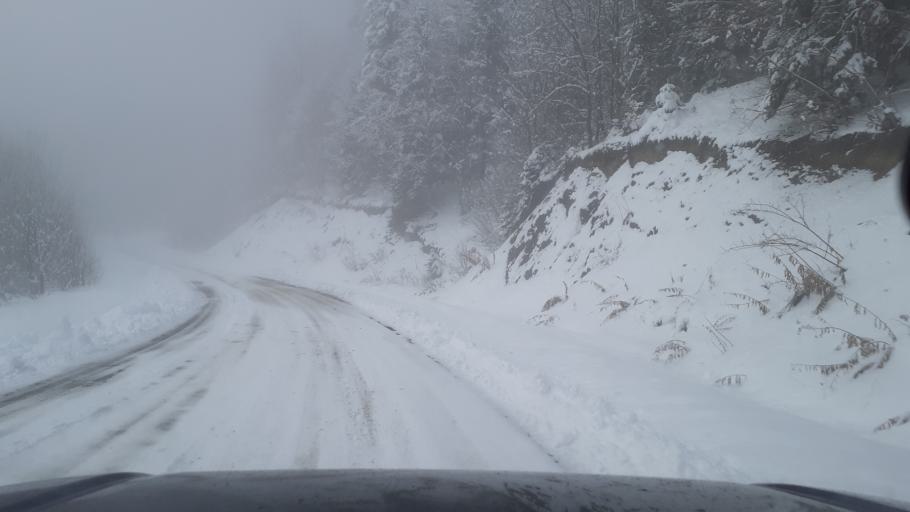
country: RU
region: Adygeya
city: Kamennomostskiy
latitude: 44.0108
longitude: 40.0306
